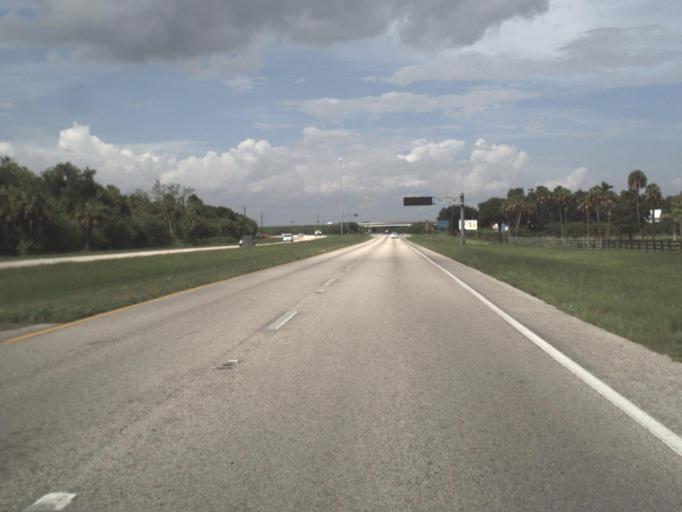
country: US
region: Florida
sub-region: Manatee County
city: Memphis
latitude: 27.5760
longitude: -82.5757
